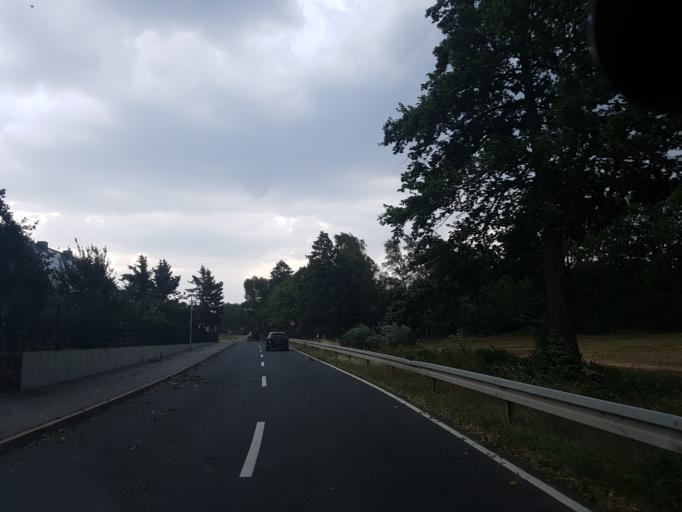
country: DE
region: Saxony
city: Ebersbach
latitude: 51.0902
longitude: 13.0841
